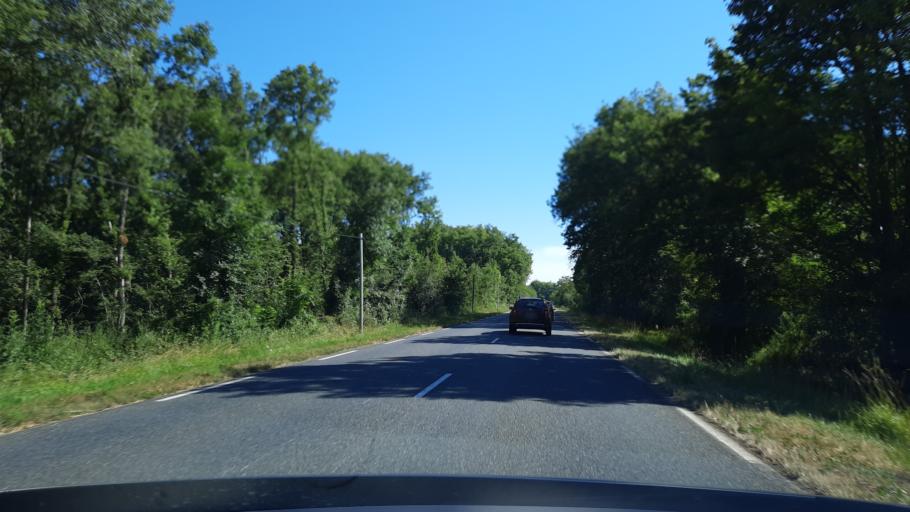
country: FR
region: Midi-Pyrenees
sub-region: Departement du Tarn-et-Garonne
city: Caylus
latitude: 44.3114
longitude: 1.8863
